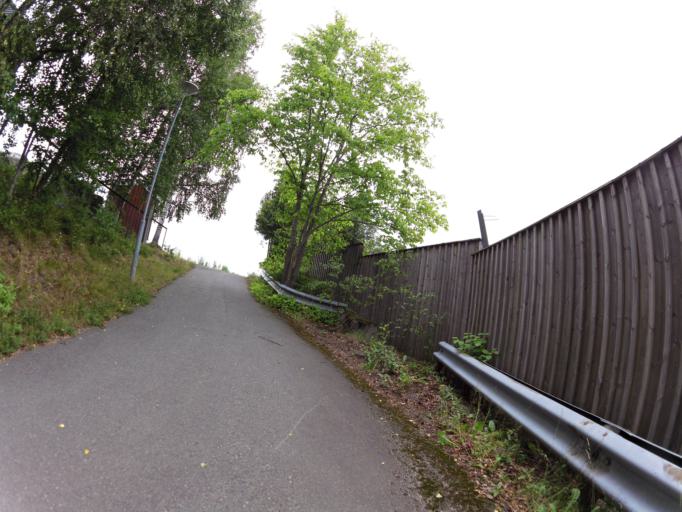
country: NO
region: Akershus
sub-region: Vestby
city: Vestby
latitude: 59.5314
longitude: 10.7496
